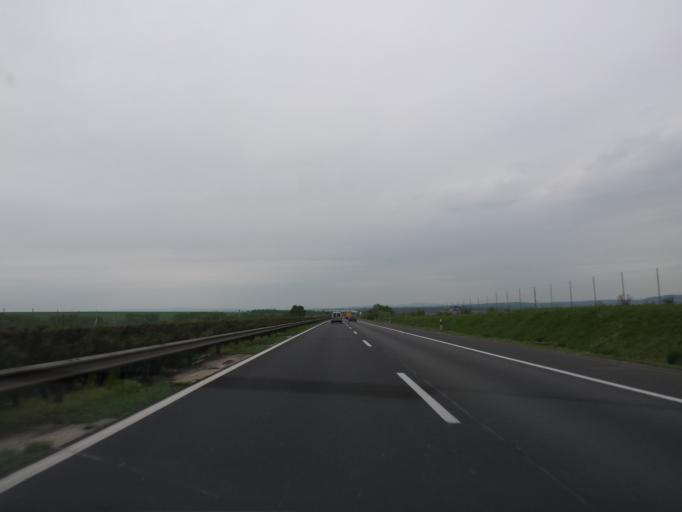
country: HU
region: Pest
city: Biatorbagy
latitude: 47.4999
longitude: 18.7929
